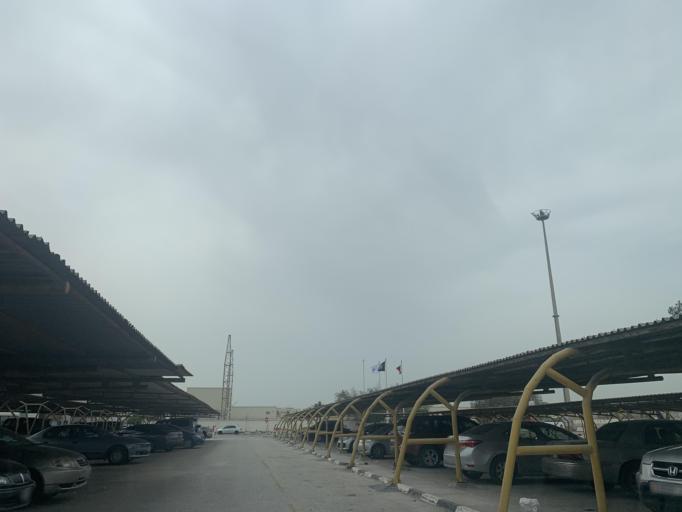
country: BH
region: Muharraq
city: Al Hadd
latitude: 26.1931
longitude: 50.6660
